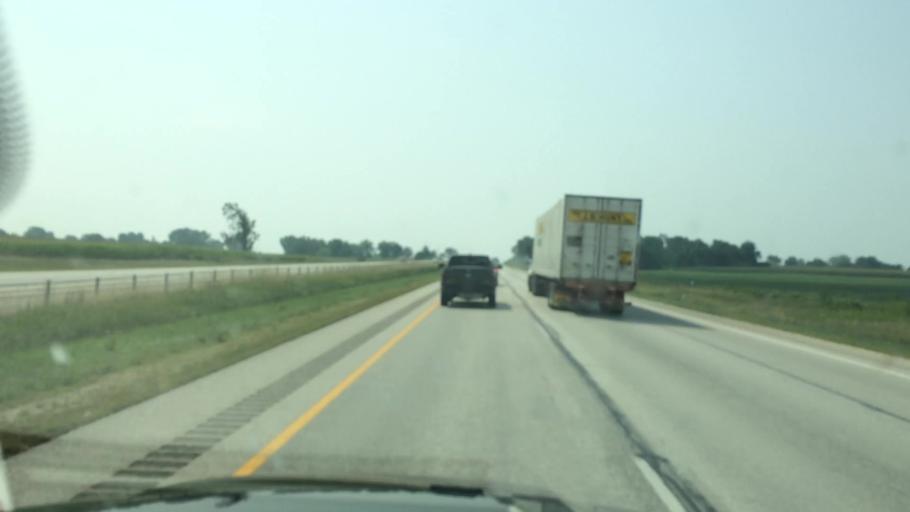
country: US
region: Wisconsin
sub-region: Dodge County
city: Lomira
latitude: 43.6823
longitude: -88.4421
